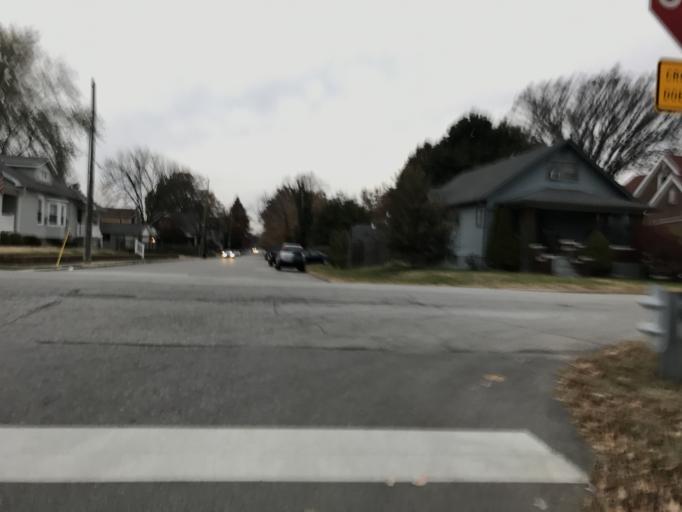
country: US
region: Kentucky
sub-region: Jefferson County
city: Audubon Park
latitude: 38.2153
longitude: -85.7370
